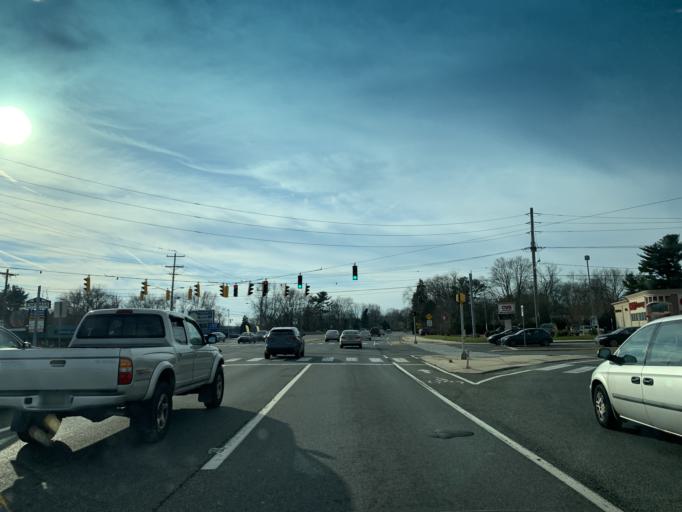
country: US
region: Delaware
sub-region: New Castle County
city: Brookside
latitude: 39.6629
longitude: -75.7260
